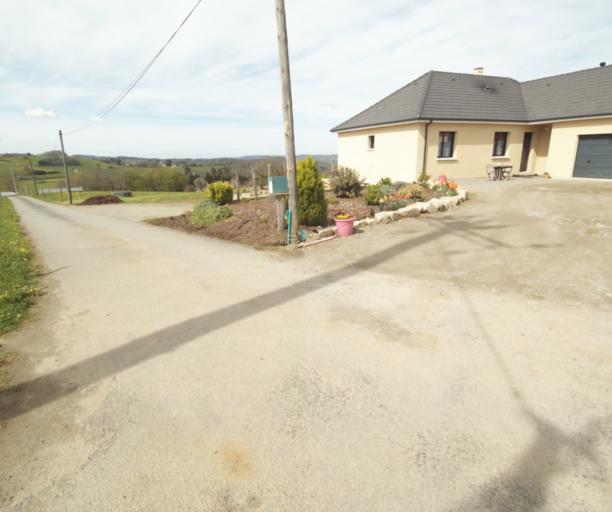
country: FR
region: Limousin
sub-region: Departement de la Correze
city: Laguenne
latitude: 45.2413
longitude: 1.8358
